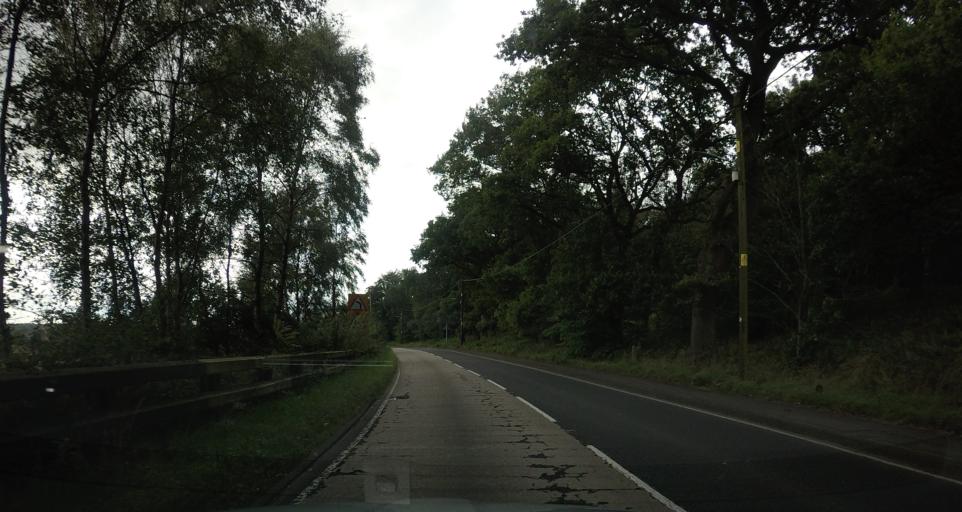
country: GB
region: Scotland
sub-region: Clackmannanshire
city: Dollar
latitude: 56.1546
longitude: -3.6286
